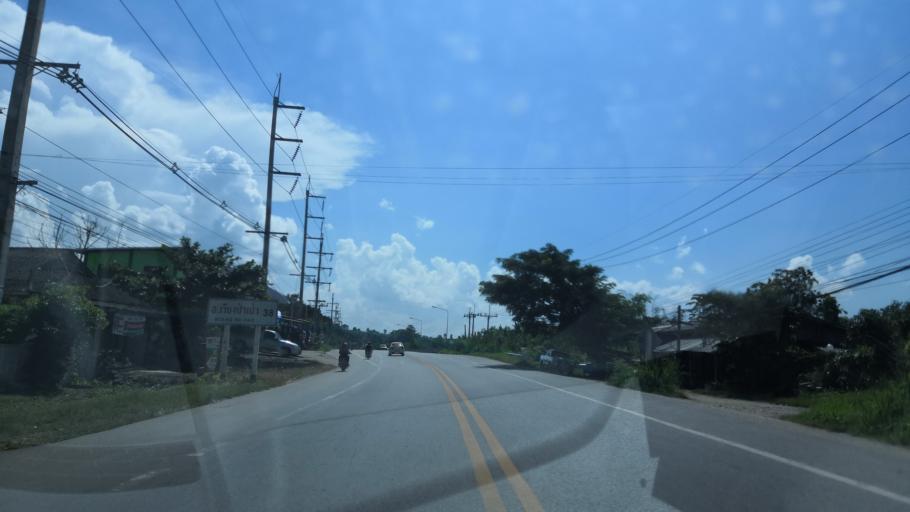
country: TH
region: Chiang Rai
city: Mae Suai
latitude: 19.6543
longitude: 99.5388
